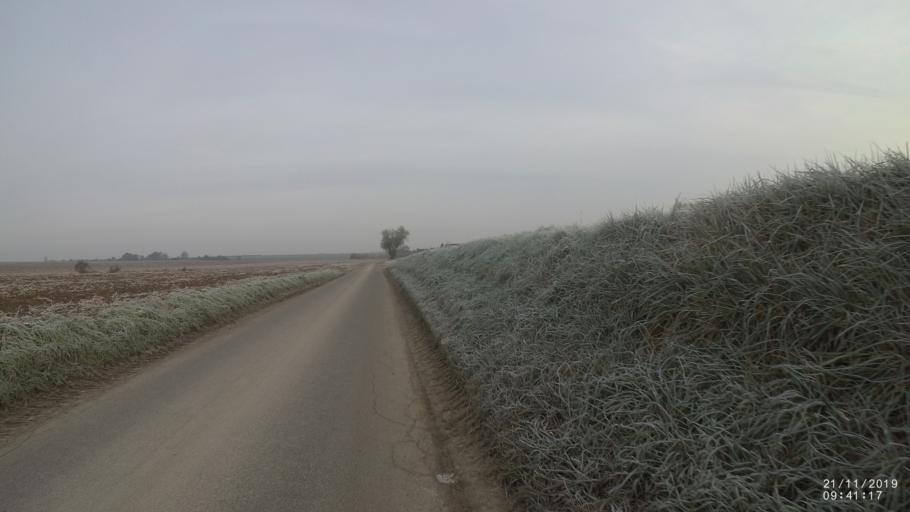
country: BE
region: Flanders
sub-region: Provincie Vlaams-Brabant
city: Tienen
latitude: 50.7780
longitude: 4.9943
